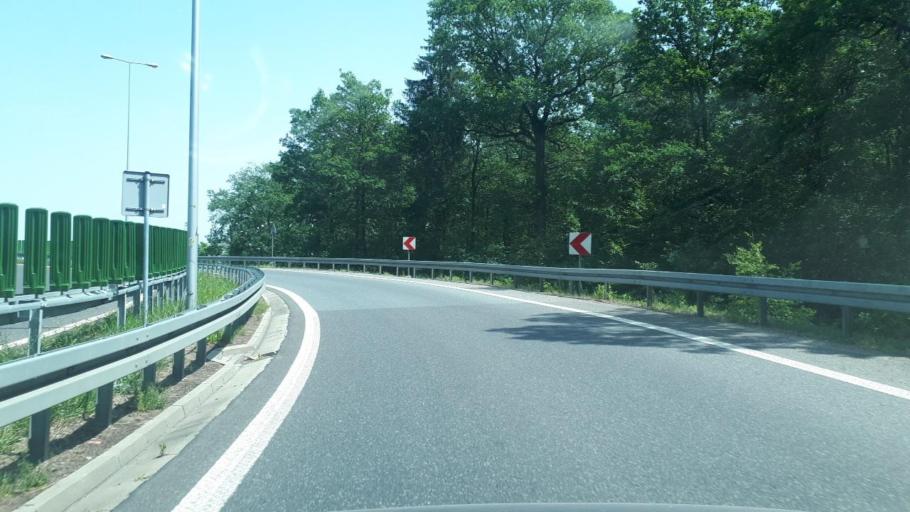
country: PL
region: Silesian Voivodeship
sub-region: Gliwice
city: Gliwice
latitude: 50.3071
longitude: 18.7189
